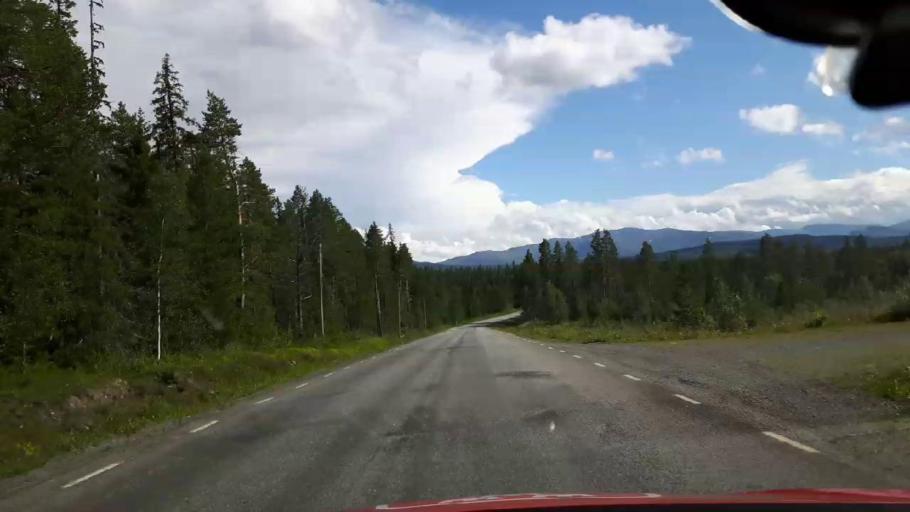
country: SE
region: Jaemtland
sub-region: Are Kommun
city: Are
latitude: 63.2236
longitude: 13.1626
